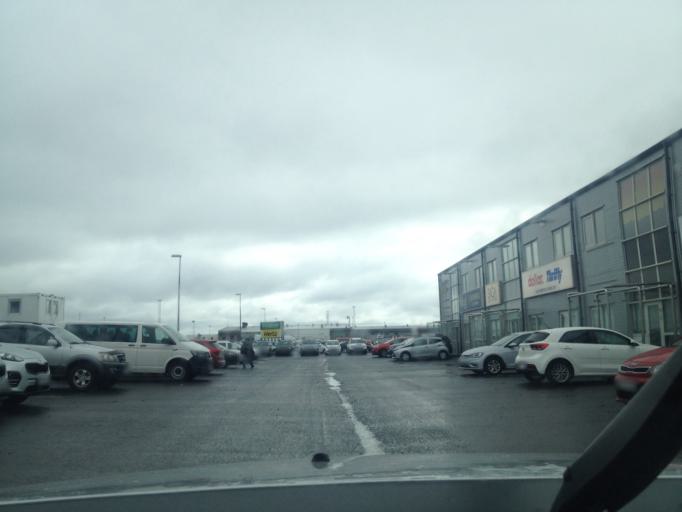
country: IS
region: Southern Peninsula
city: Reykjanesbaer
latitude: 63.9986
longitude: -22.6299
